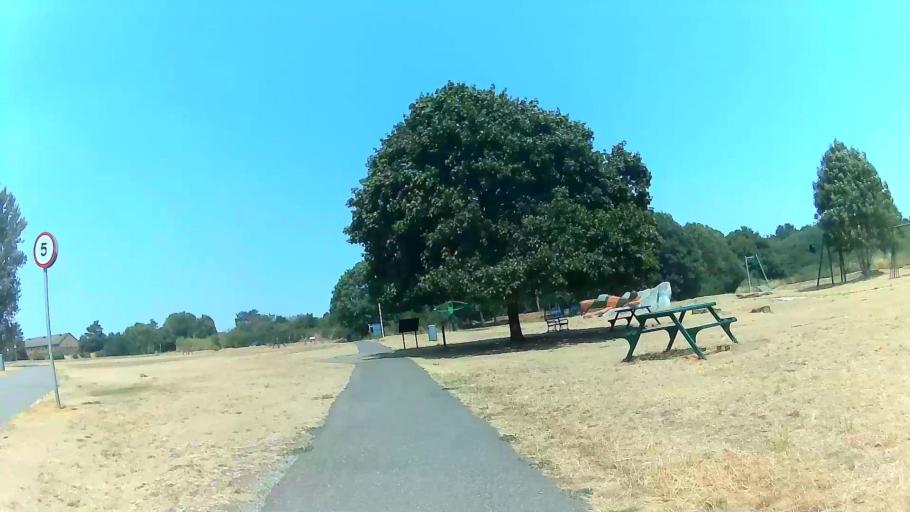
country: GB
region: England
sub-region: Greater London
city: Hornchurch
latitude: 51.5416
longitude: 0.2147
